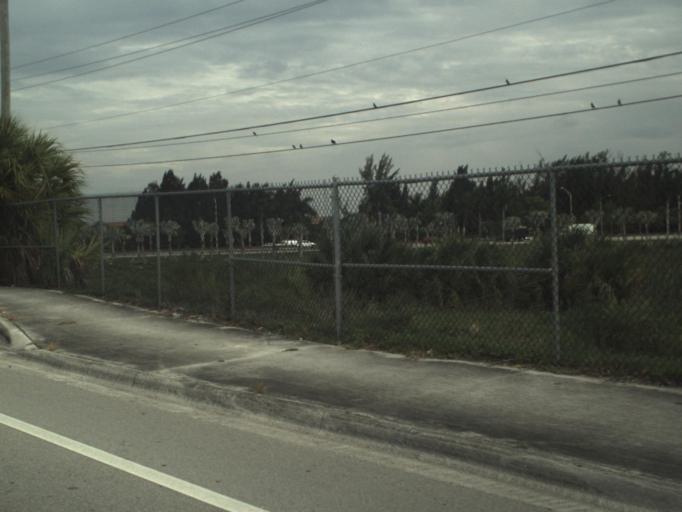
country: US
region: Florida
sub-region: Palm Beach County
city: Plantation Mobile Home Park
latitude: 26.7077
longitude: -80.1384
